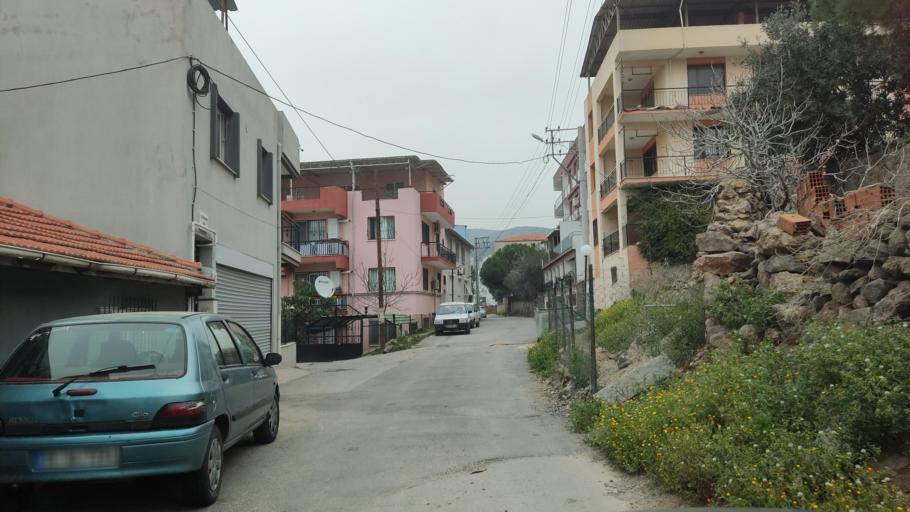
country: TR
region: Izmir
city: Karsiyaka
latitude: 38.4940
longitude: 27.0664
